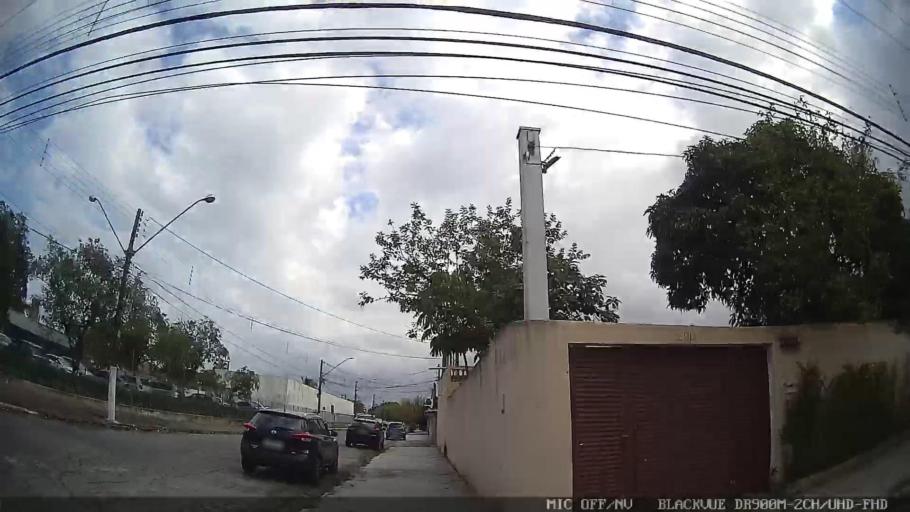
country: BR
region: Sao Paulo
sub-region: Guaruja
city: Guaruja
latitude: -23.9951
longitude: -46.2732
